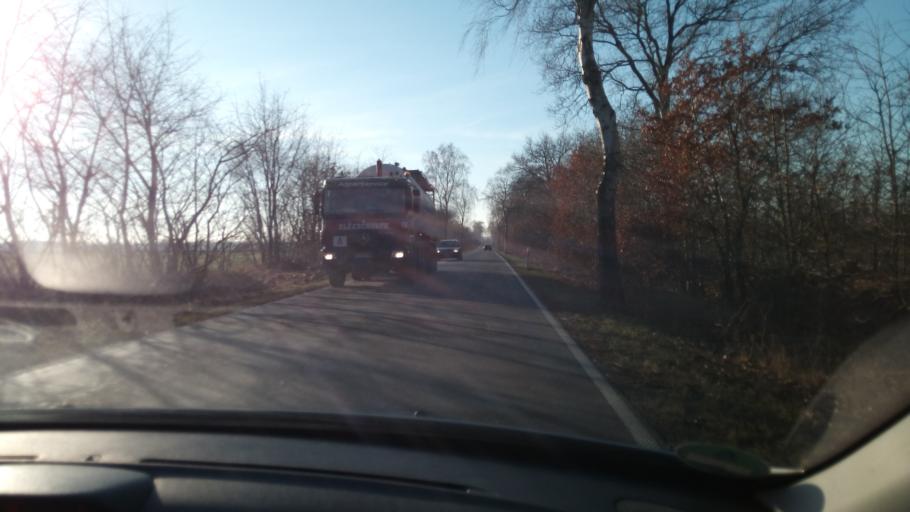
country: DE
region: Schleswig-Holstein
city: Brothen
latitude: 53.4904
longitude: 10.6630
